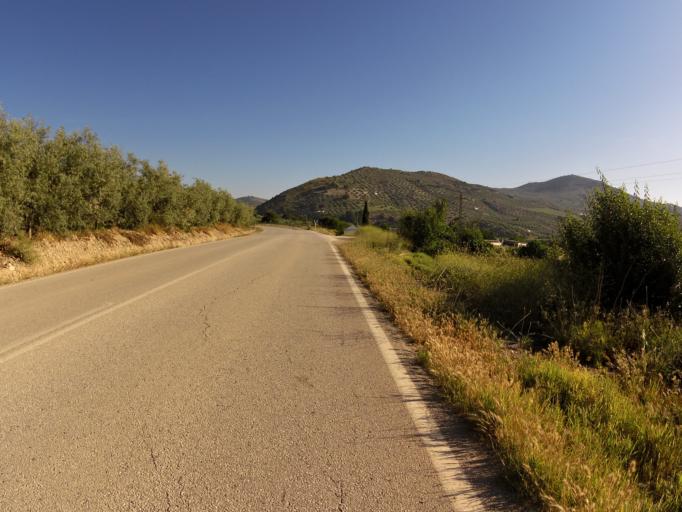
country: ES
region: Andalusia
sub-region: Provincia de Granada
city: Huetor-Tajar
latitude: 37.2373
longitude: -4.0769
